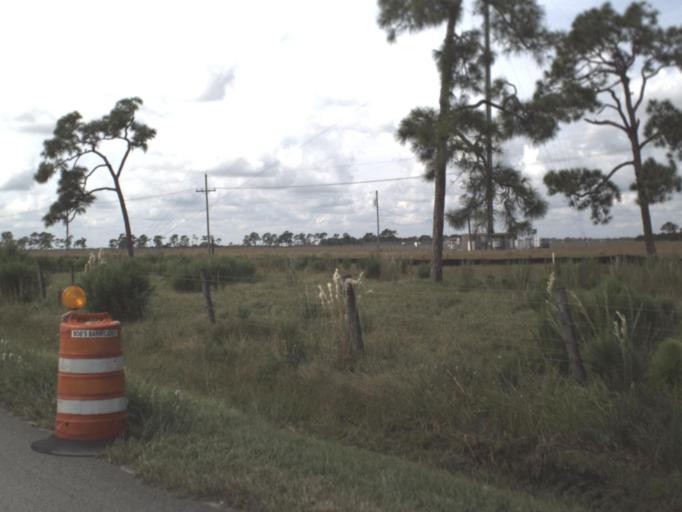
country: US
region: Florida
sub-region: Okeechobee County
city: Taylor Creek
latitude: 27.2865
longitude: -80.7042
